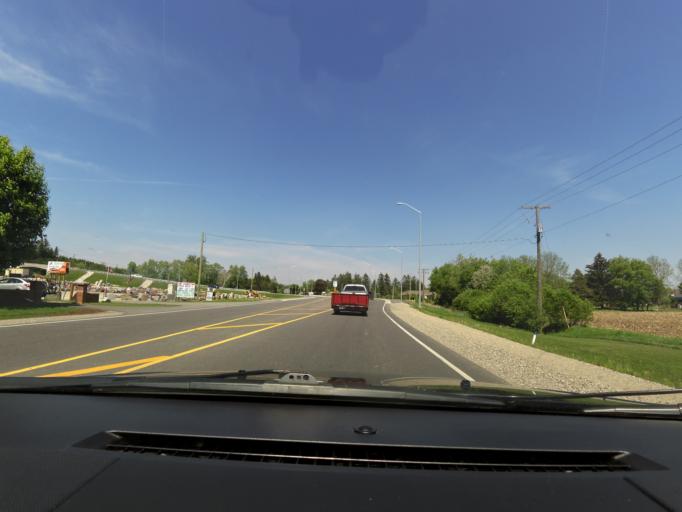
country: CA
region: Ontario
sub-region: Wellington County
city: Guelph
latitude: 43.5784
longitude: -80.1878
